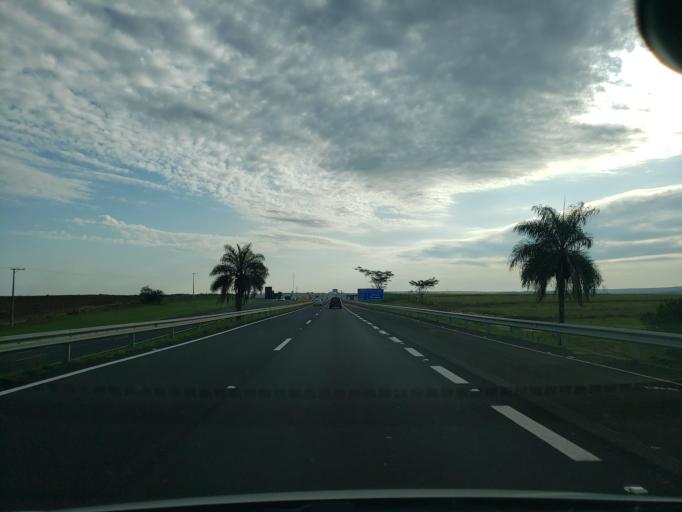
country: BR
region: Sao Paulo
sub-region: Guararapes
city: Guararapes
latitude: -21.2109
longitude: -50.7262
